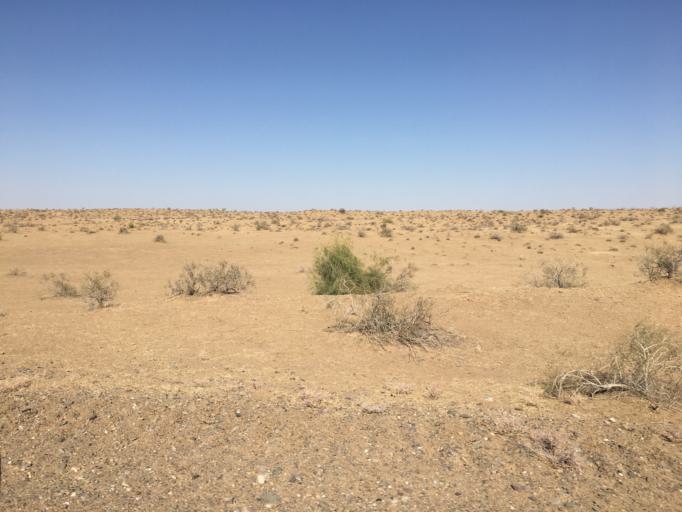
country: IR
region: Razavi Khorasan
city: Sarakhs
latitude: 36.7653
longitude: 61.3241
